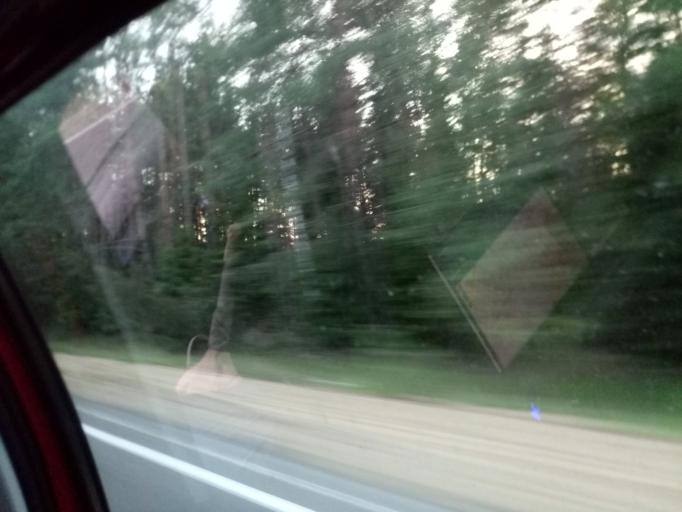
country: RU
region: Moskovskaya
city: Noginsk-9
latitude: 56.0751
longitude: 38.5693
